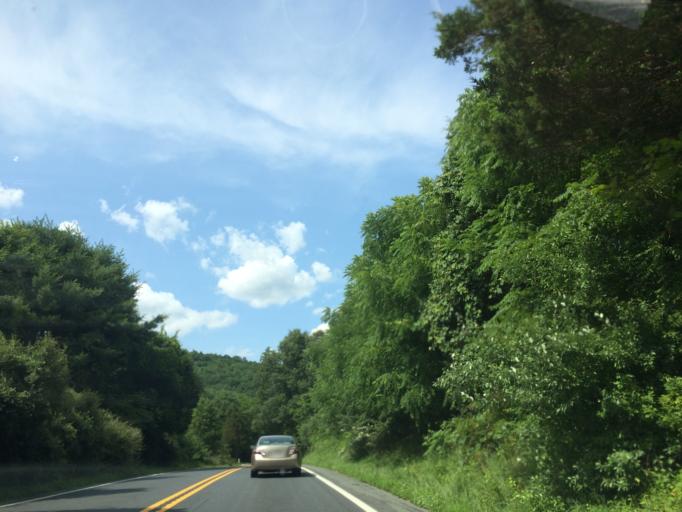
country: US
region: Pennsylvania
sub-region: Pike County
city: Birchwood Lakes
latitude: 41.1968
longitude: -74.8839
